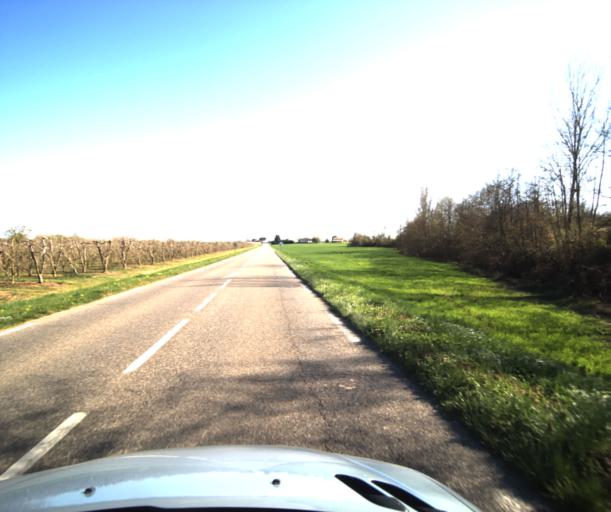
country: FR
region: Midi-Pyrenees
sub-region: Departement du Tarn-et-Garonne
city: Bressols
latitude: 43.9516
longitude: 1.3485
